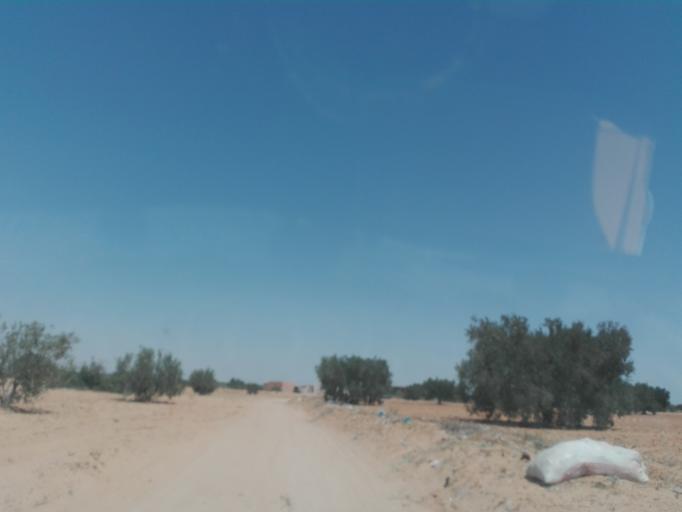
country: TN
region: Safaqis
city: Bi'r `Ali Bin Khalifah
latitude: 34.6728
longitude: 10.2328
